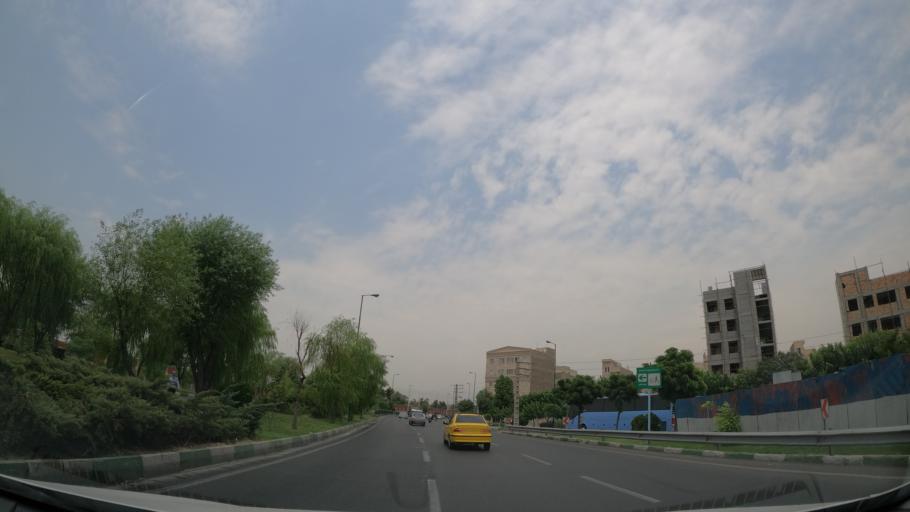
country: IR
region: Tehran
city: Tehran
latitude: 35.6838
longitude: 51.3430
